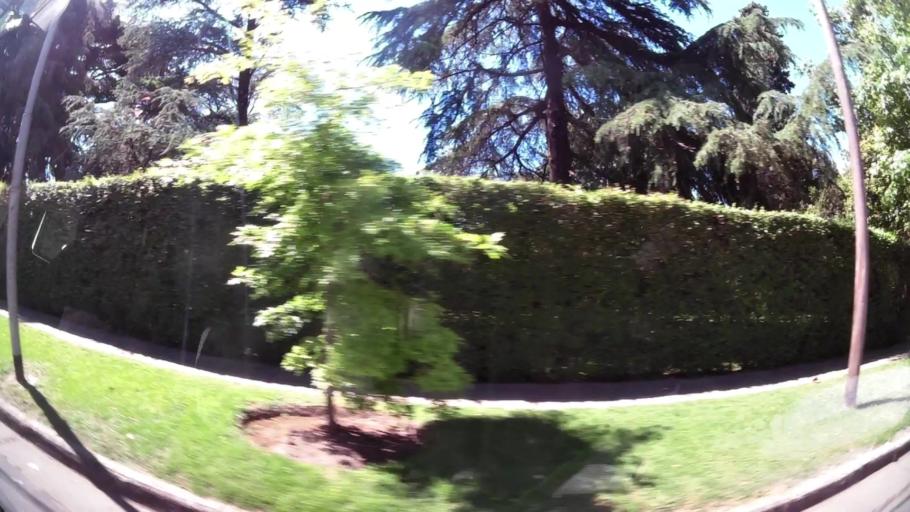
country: AR
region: Buenos Aires
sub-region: Partido de Tigre
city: Tigre
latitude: -34.4964
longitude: -58.6226
